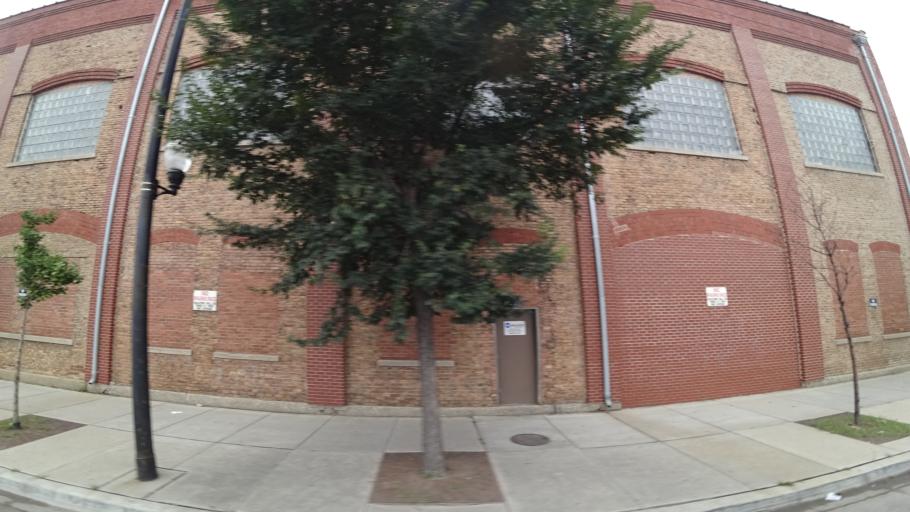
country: US
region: Illinois
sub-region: Cook County
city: Chicago
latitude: 41.8469
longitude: -87.6660
